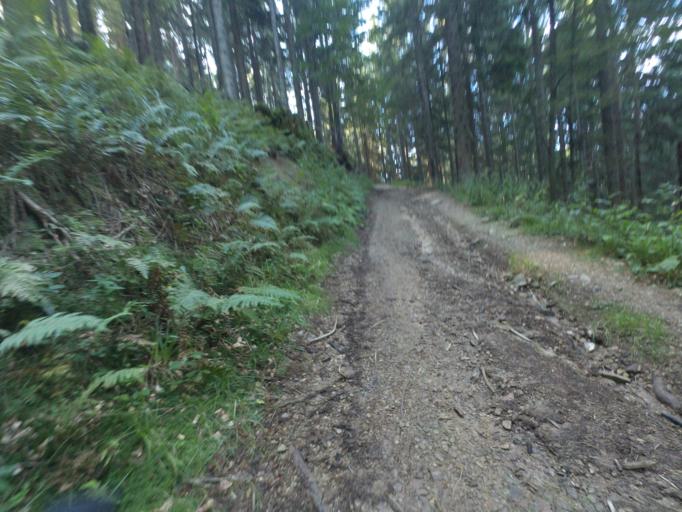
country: AT
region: Salzburg
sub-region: Politischer Bezirk Salzburg-Umgebung
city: Hintersee
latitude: 47.6963
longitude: 13.2530
